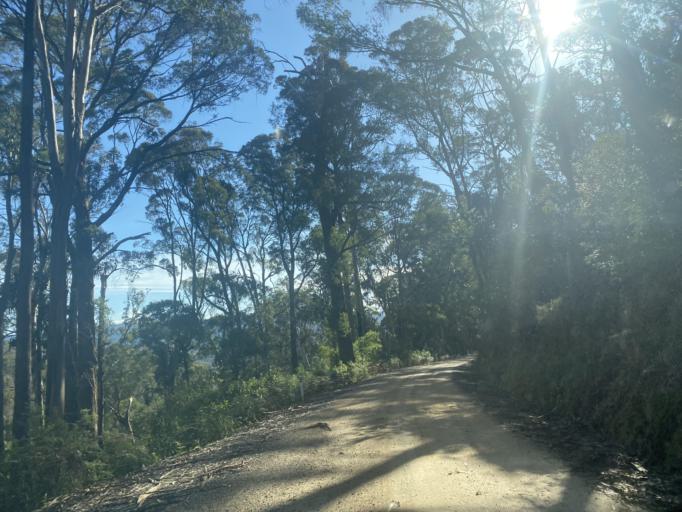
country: AU
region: Victoria
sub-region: Mansfield
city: Mansfield
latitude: -36.8449
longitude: 146.1704
